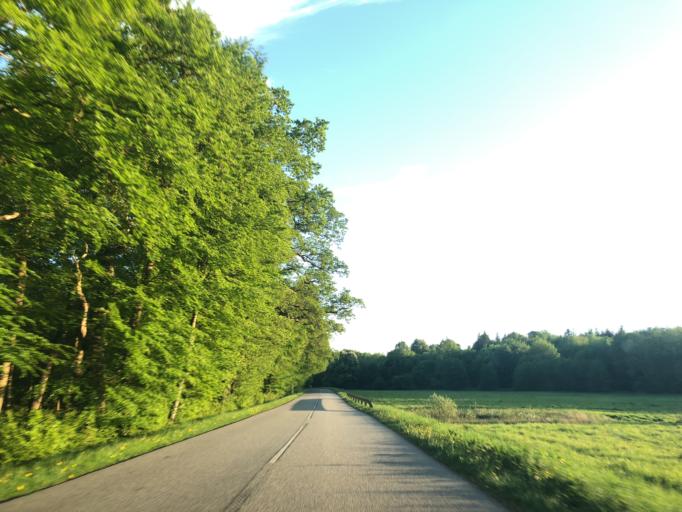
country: DK
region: Zealand
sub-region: Koge Kommune
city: Borup
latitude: 55.4331
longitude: 11.9387
